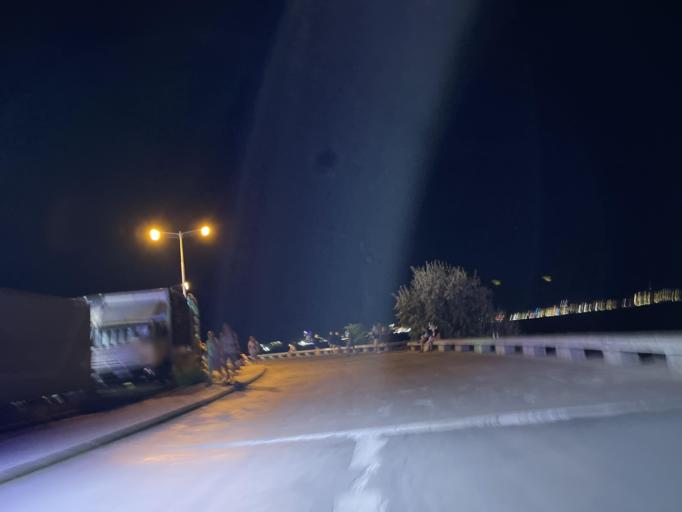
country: BG
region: Burgas
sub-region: Obshtina Nesebur
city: Nesebar
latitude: 42.6610
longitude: 27.7246
